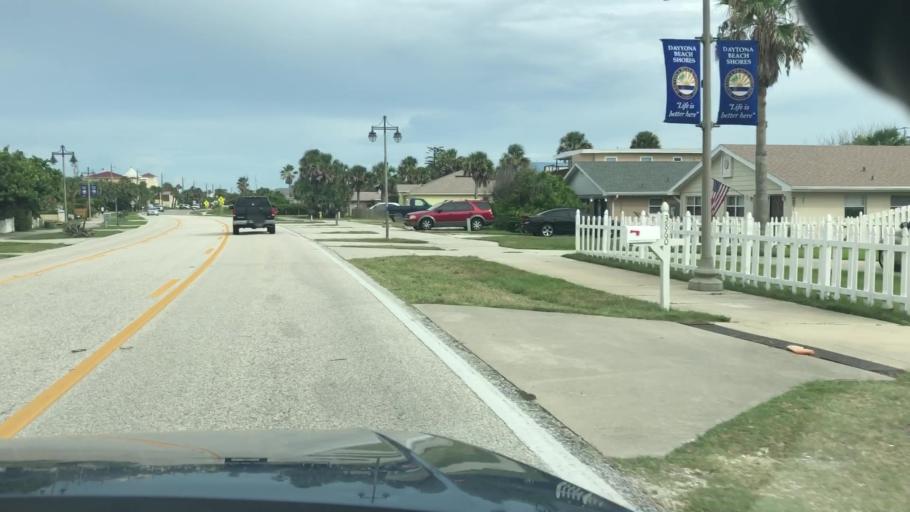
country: US
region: Florida
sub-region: Volusia County
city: Port Orange
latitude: 29.1375
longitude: -80.9617
